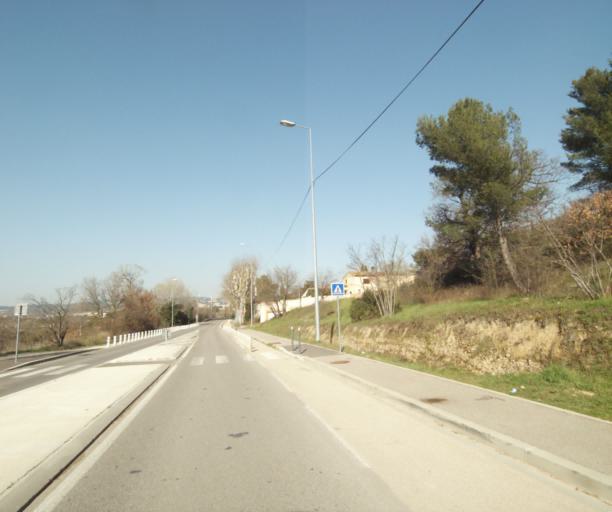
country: FR
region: Provence-Alpes-Cote d'Azur
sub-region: Departement des Bouches-du-Rhone
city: Aix-en-Provence
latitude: 43.5042
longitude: 5.4354
